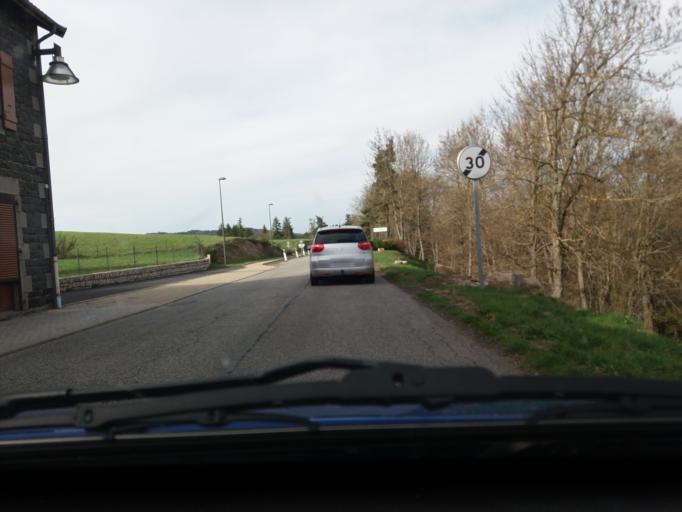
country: FR
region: Auvergne
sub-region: Departement de la Haute-Loire
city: Mazet-Saint-Voy
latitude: 45.0495
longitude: 4.2465
